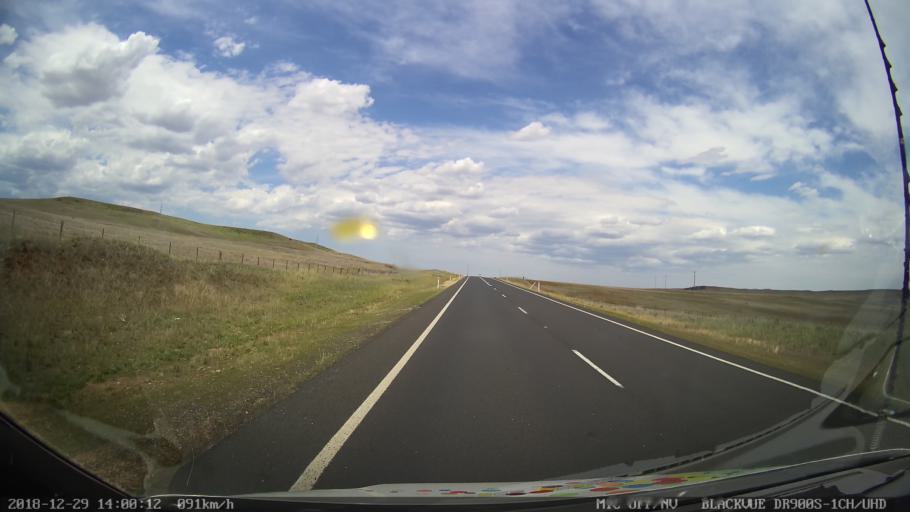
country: AU
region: New South Wales
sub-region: Cooma-Monaro
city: Cooma
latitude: -36.2618
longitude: 149.1556
